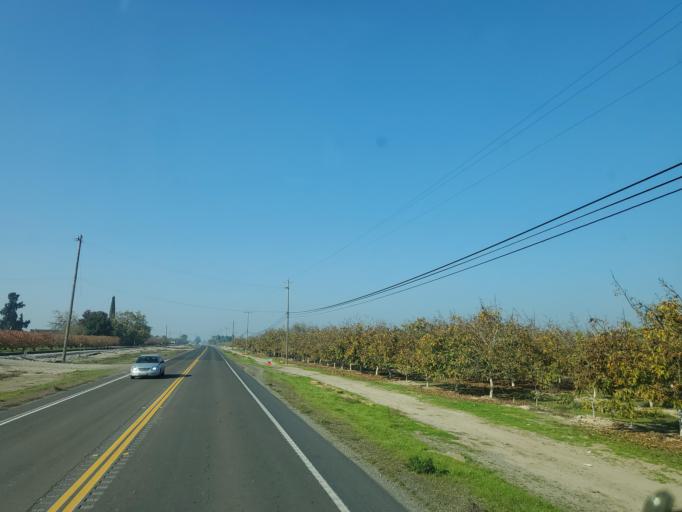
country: US
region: California
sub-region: San Joaquin County
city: Manteca
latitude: 37.8341
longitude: -121.1551
